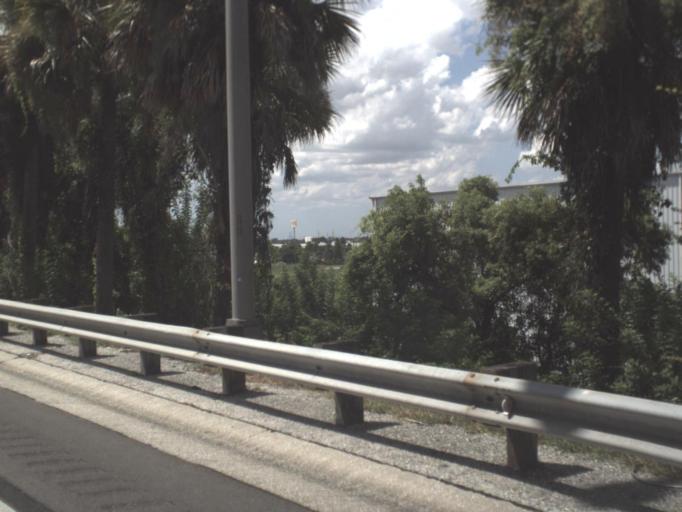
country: US
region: Florida
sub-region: Hillsborough County
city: Palm River-Clair Mel
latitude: 27.9500
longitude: -82.3966
